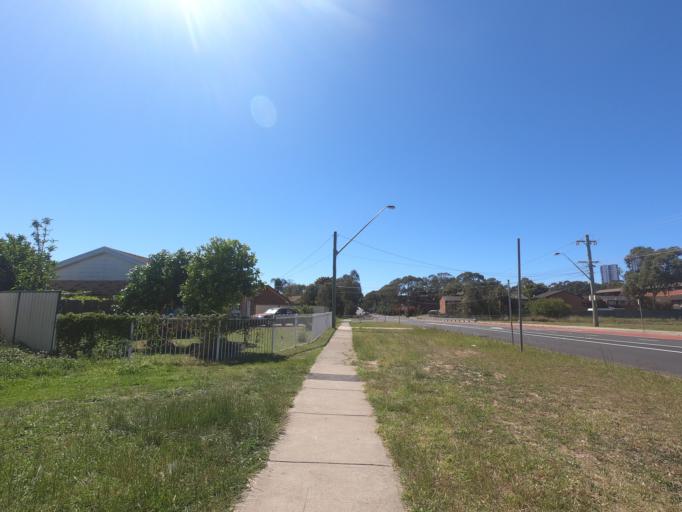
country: AU
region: New South Wales
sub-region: Fairfield
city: Cabramatta West
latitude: -33.9213
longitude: 150.9143
